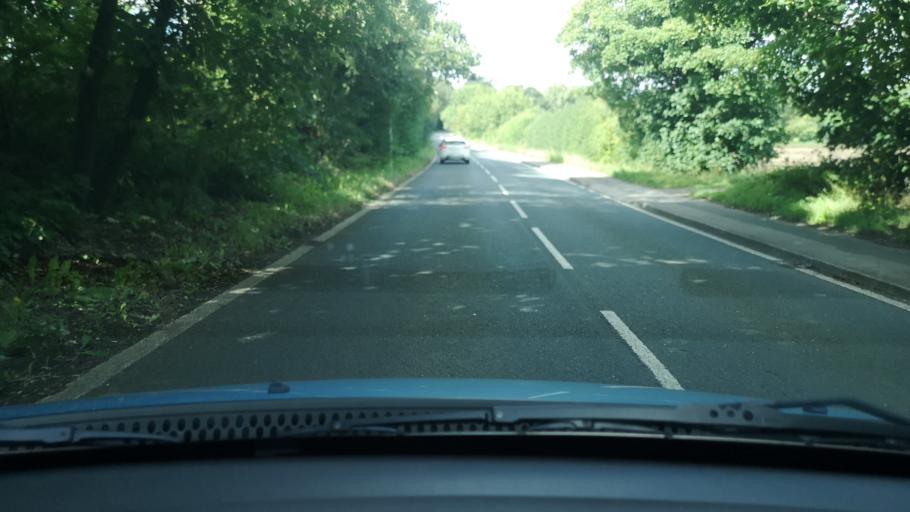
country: GB
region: England
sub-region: City and Borough of Wakefield
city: Featherstone
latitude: 53.6928
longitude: -1.3687
